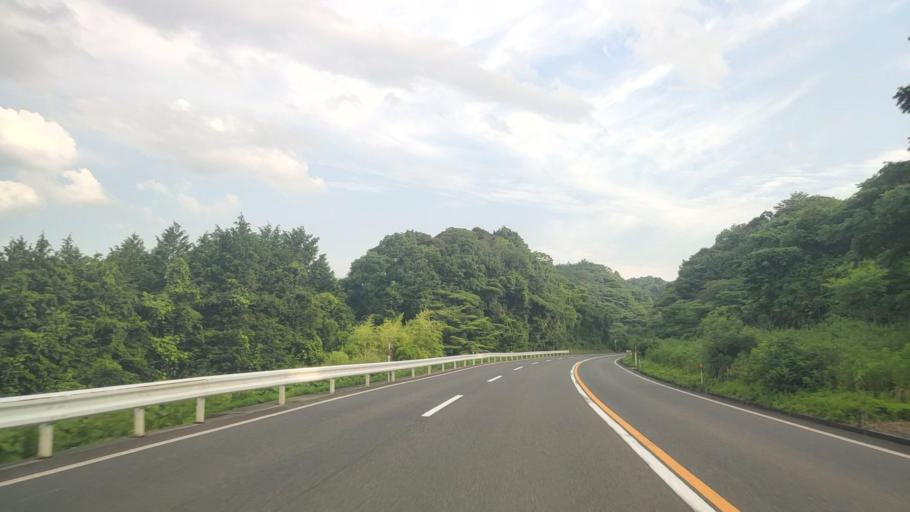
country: JP
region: Tottori
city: Kurayoshi
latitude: 35.3502
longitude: 133.7502
